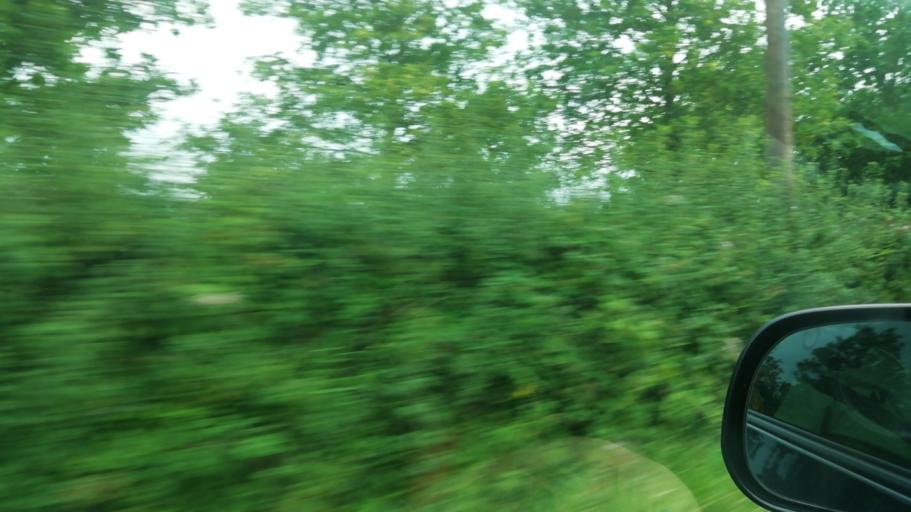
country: IE
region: Munster
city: Fethard
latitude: 52.4796
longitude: -7.6928
